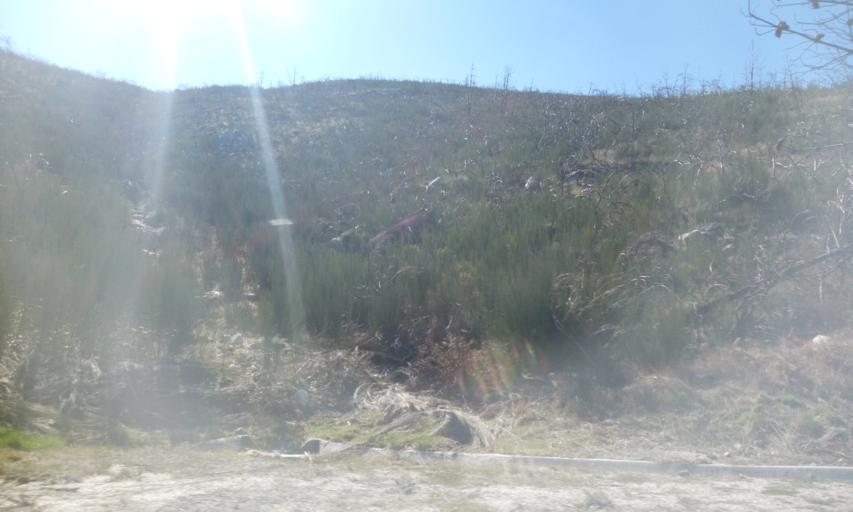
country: PT
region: Guarda
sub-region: Manteigas
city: Manteigas
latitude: 40.4902
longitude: -7.5406
